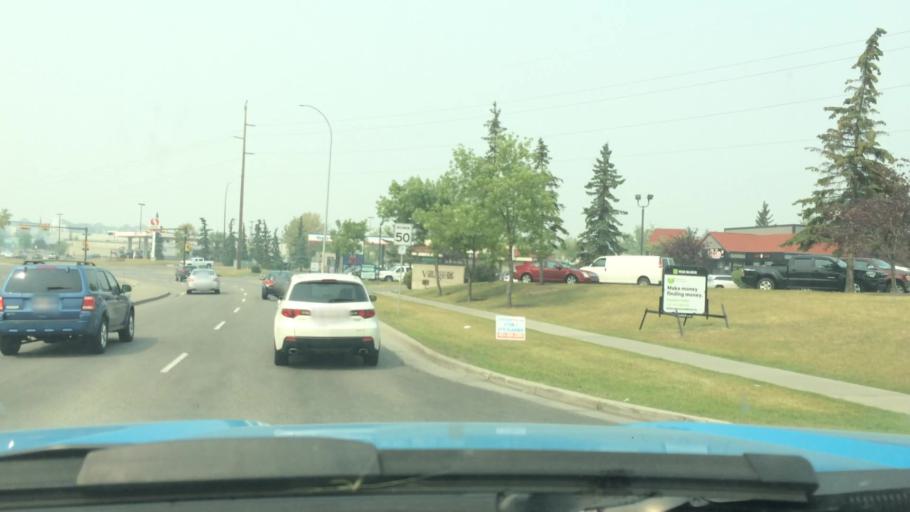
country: CA
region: Alberta
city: Calgary
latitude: 51.1245
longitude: -114.1984
